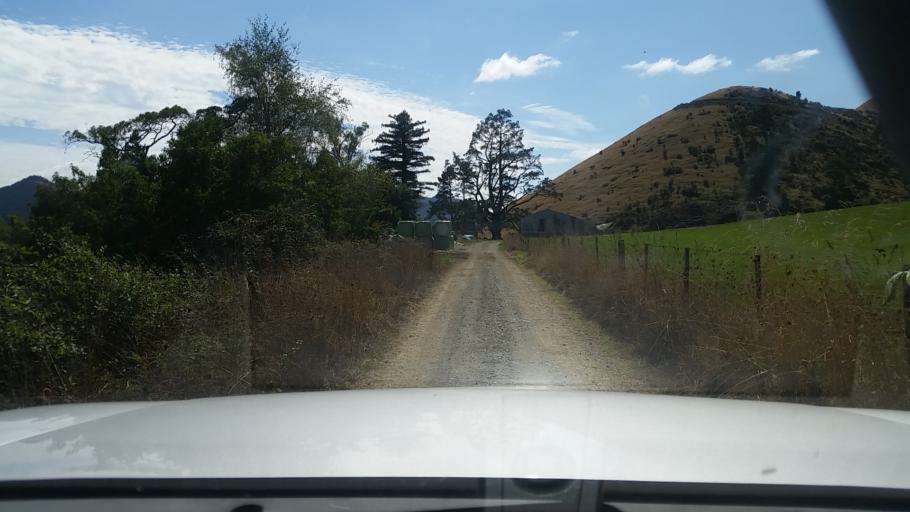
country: NZ
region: Nelson
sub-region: Nelson City
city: Nelson
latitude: -41.2481
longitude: 173.5854
